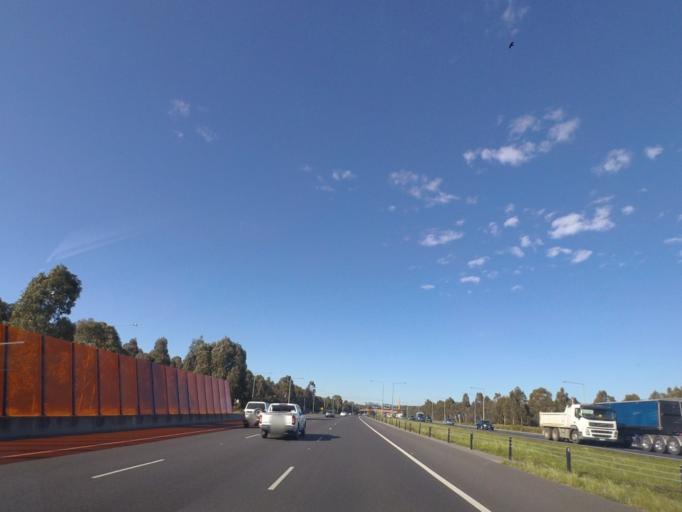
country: AU
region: Victoria
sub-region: Knox
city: Wantirna
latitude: -37.8478
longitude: 145.2168
